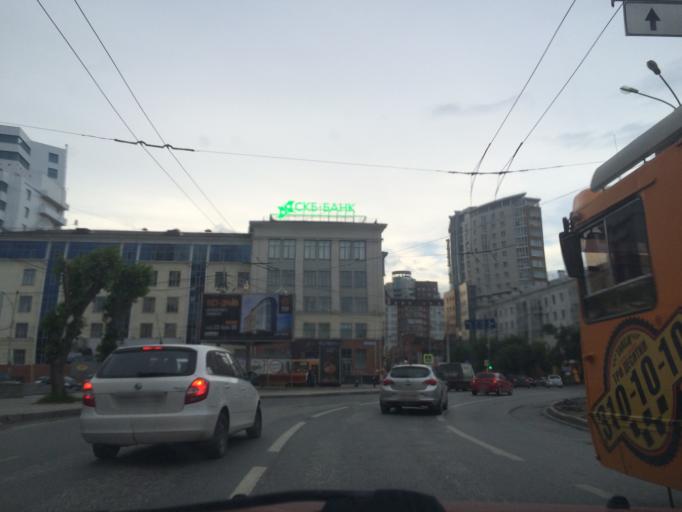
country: RU
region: Sverdlovsk
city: Yekaterinburg
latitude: 56.8280
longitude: 60.6166
